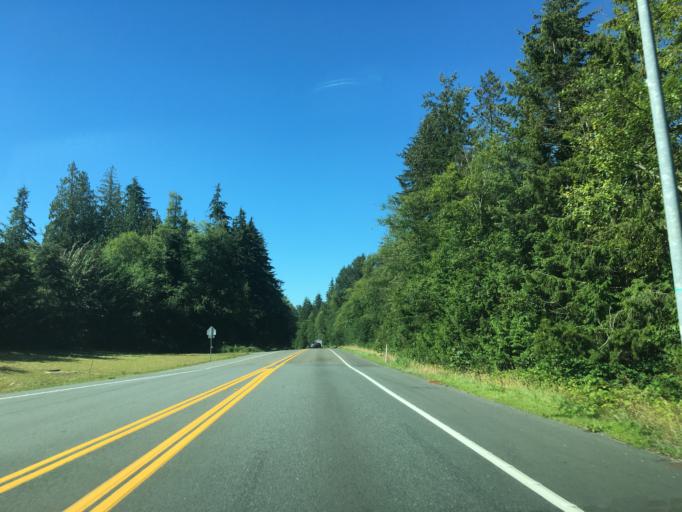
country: US
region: Washington
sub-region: Snohomish County
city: Arlington
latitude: 48.1654
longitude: -122.1193
